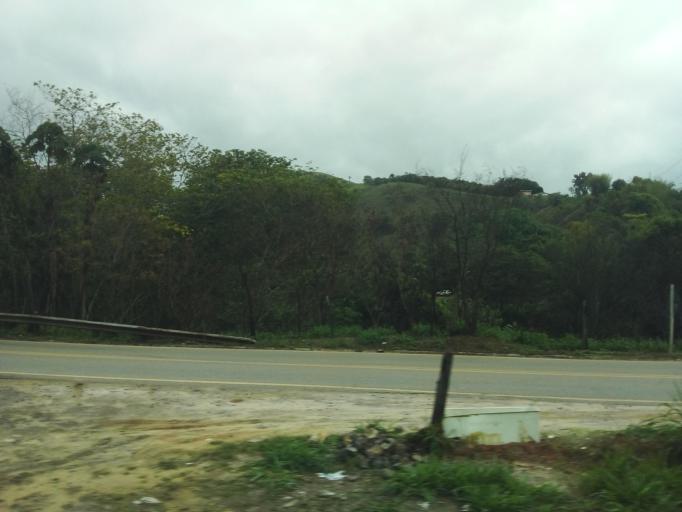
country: BR
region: Minas Gerais
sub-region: Rio Piracicaba
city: Rio Piracicaba
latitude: -19.9382
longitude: -43.1779
